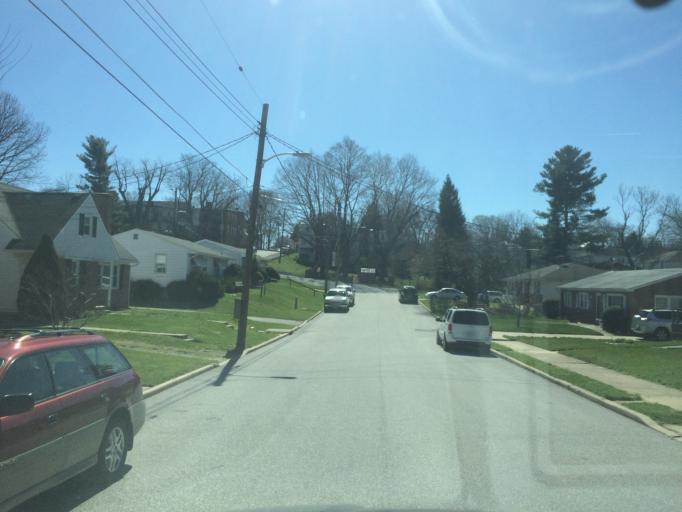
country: US
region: Maryland
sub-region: Carroll County
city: Westminster
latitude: 39.5758
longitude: -77.0012
